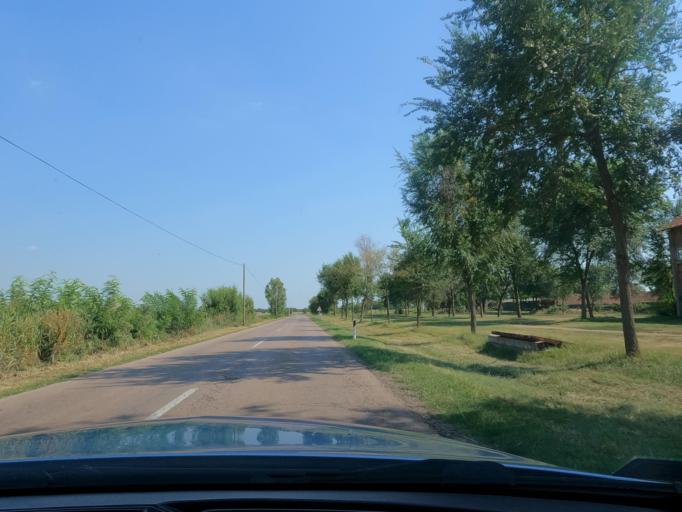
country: RS
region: Autonomna Pokrajina Vojvodina
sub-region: Severnobacki Okrug
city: Mali Igos
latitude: 45.7676
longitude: 19.7389
